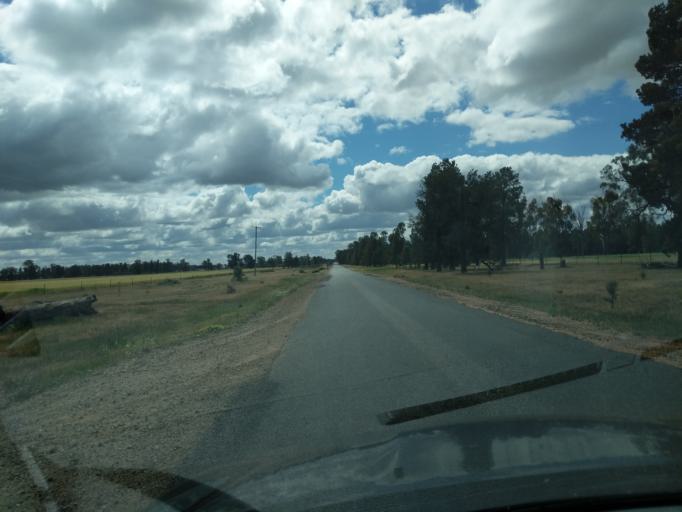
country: AU
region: New South Wales
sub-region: Coolamon
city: Coolamon
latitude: -34.8554
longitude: 146.8990
